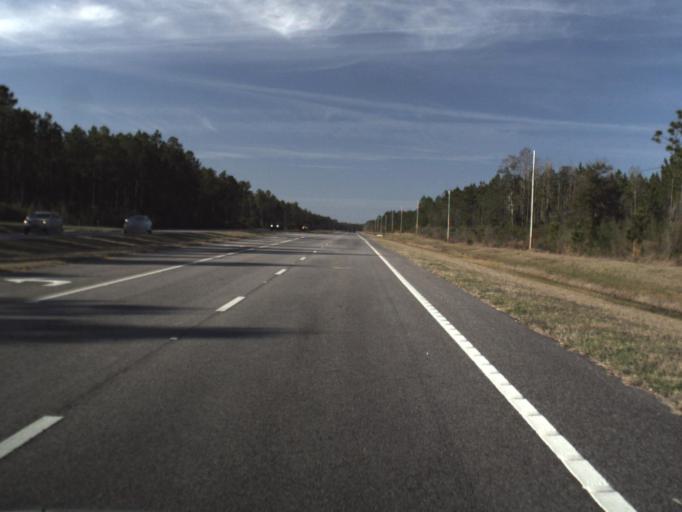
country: US
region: Florida
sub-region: Bay County
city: Laguna Beach
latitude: 30.3672
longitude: -85.8600
